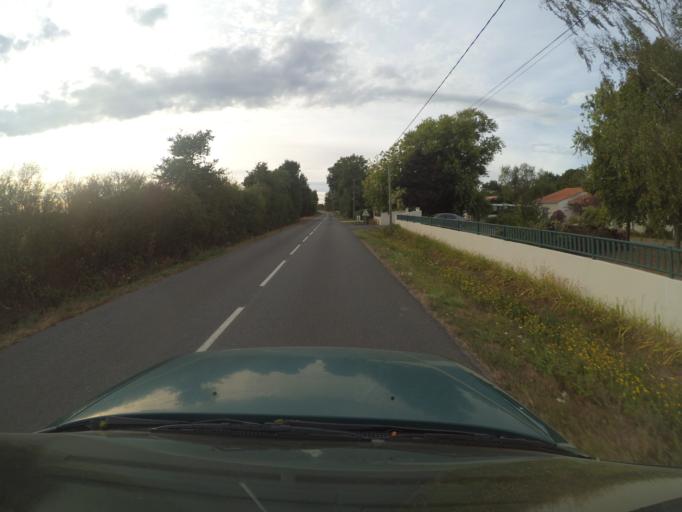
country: FR
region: Pays de la Loire
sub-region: Departement de la Vendee
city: Saint-Andre-Treize-Voies
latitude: 46.9004
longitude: -1.4328
